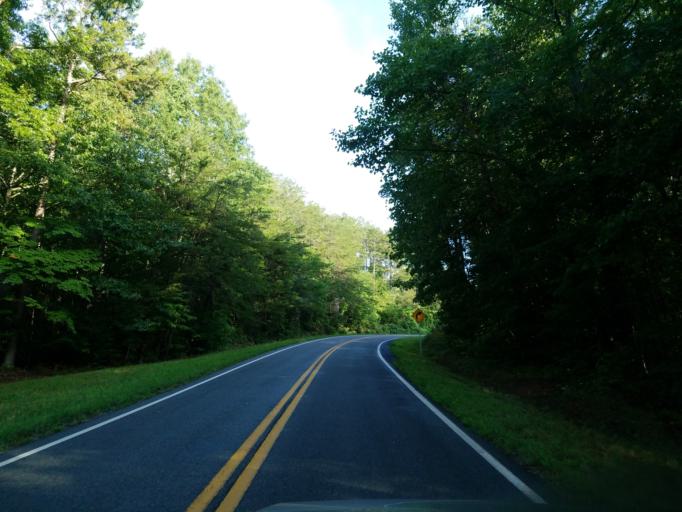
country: US
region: Georgia
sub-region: Lumpkin County
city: Dahlonega
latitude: 34.5708
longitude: -83.8927
